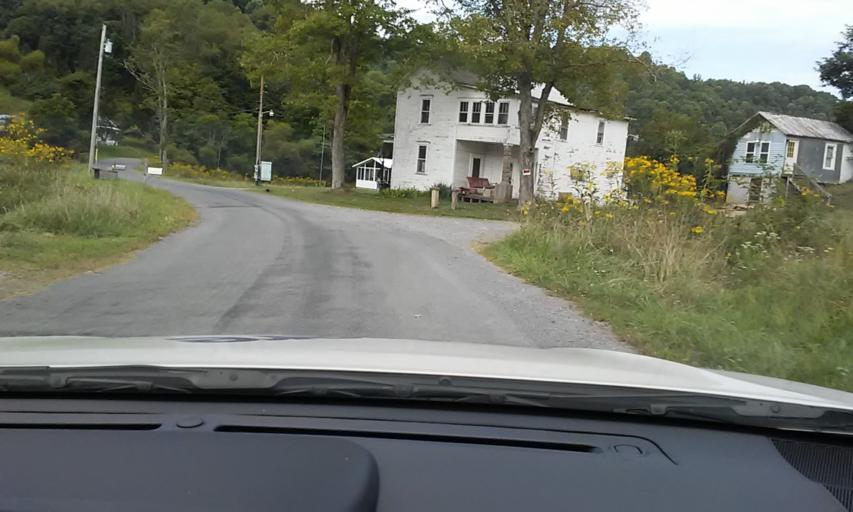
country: US
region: West Virginia
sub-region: Marion County
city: Mannington
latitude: 39.6218
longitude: -80.3515
